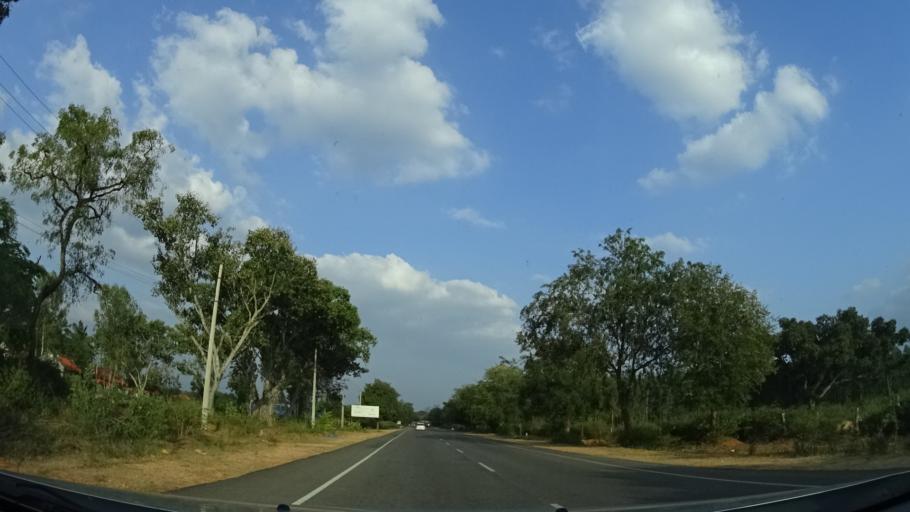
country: IN
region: Karnataka
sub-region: Mandya
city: Malavalli
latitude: 12.3726
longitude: 77.0266
